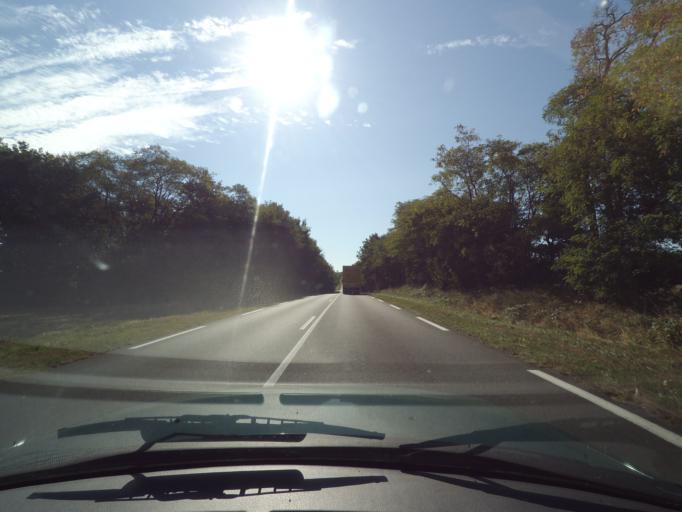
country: FR
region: Poitou-Charentes
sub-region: Departement de la Vienne
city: Terce
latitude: 46.4290
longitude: 0.6156
